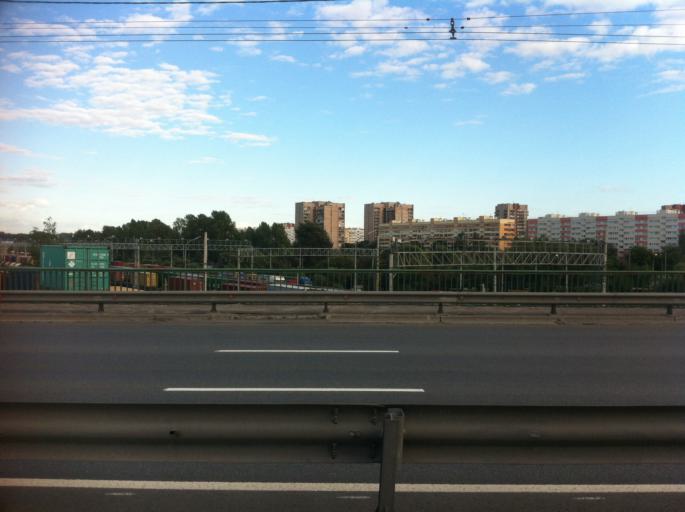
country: RU
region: St.-Petersburg
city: Avtovo
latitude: 59.8653
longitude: 30.2412
